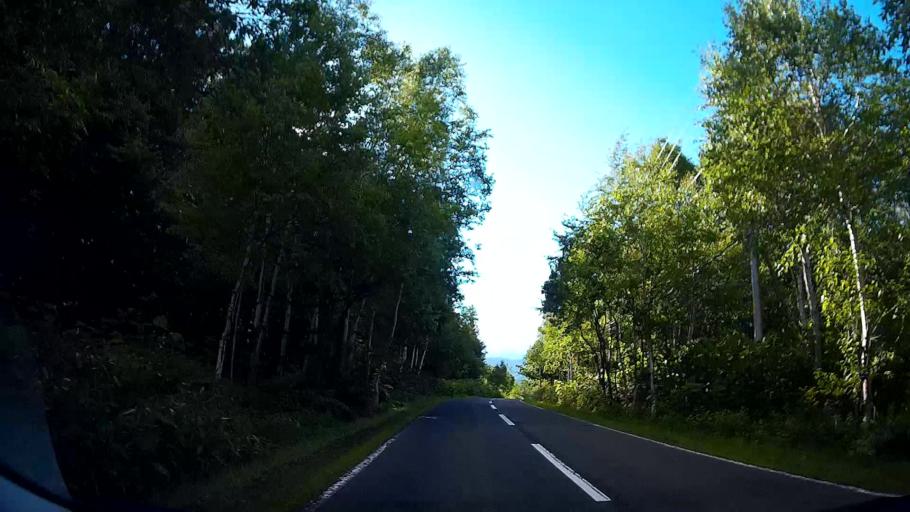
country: JP
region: Hokkaido
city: Sapporo
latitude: 42.9722
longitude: 141.1481
